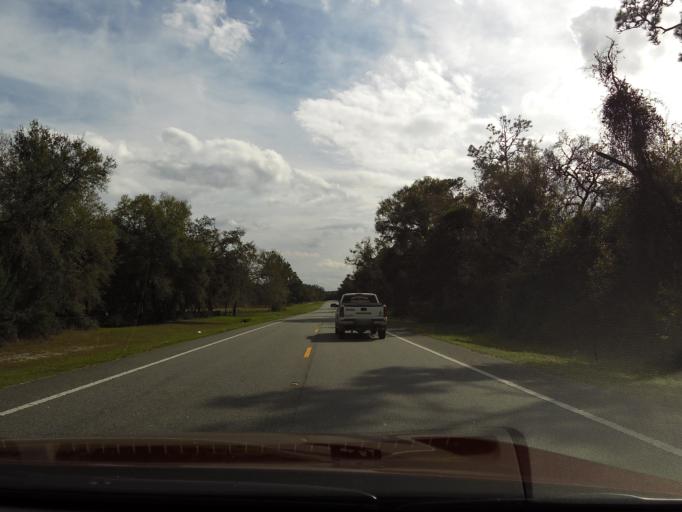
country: US
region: Florida
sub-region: Volusia County
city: De Leon Springs
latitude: 29.1807
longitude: -81.3039
